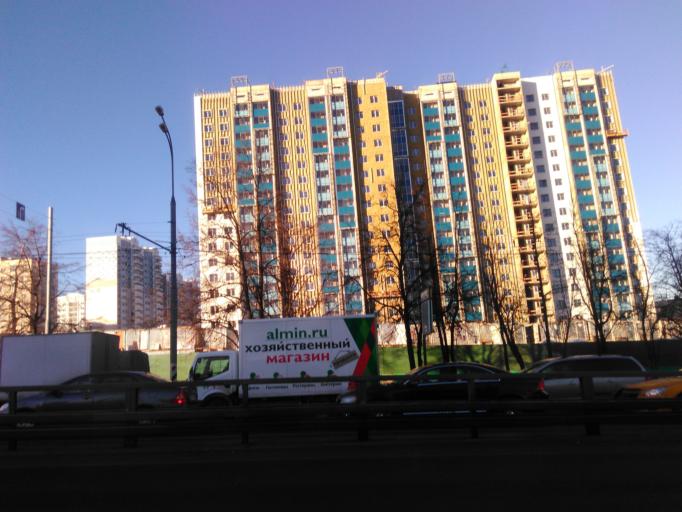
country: RU
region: Moskovskaya
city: Cheremushki
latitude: 55.6507
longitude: 37.5337
